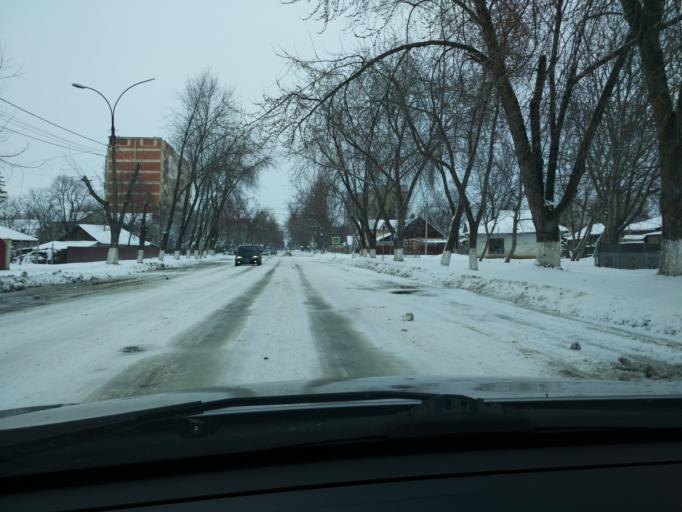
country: MD
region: Ungheni
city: Ungheni
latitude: 47.2068
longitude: 27.7936
